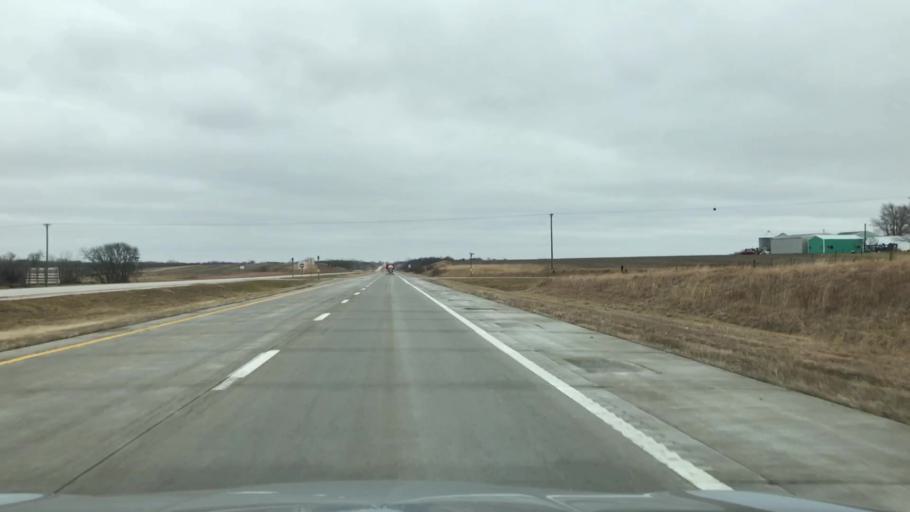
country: US
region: Missouri
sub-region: Caldwell County
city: Hamilton
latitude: 39.7337
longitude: -93.9855
